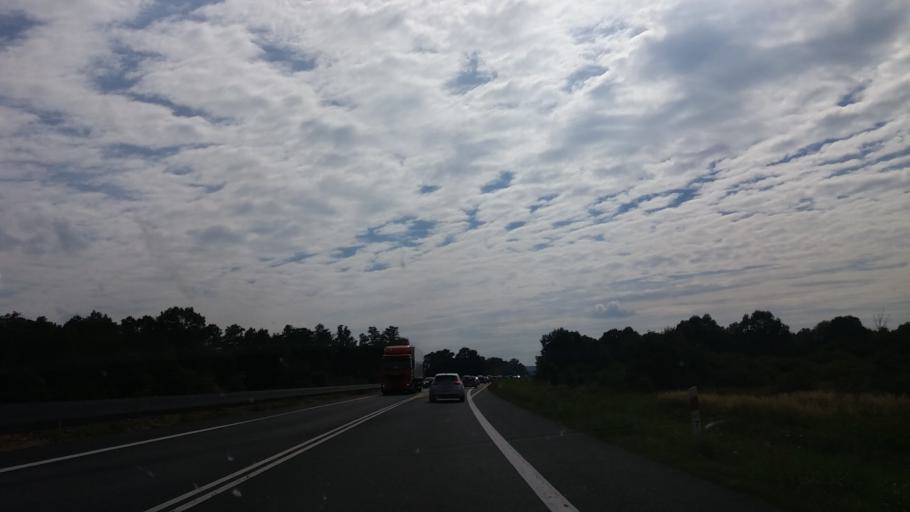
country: PL
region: Lubusz
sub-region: Powiat zielonogorski
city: Sulechow
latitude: 52.0173
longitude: 15.6274
